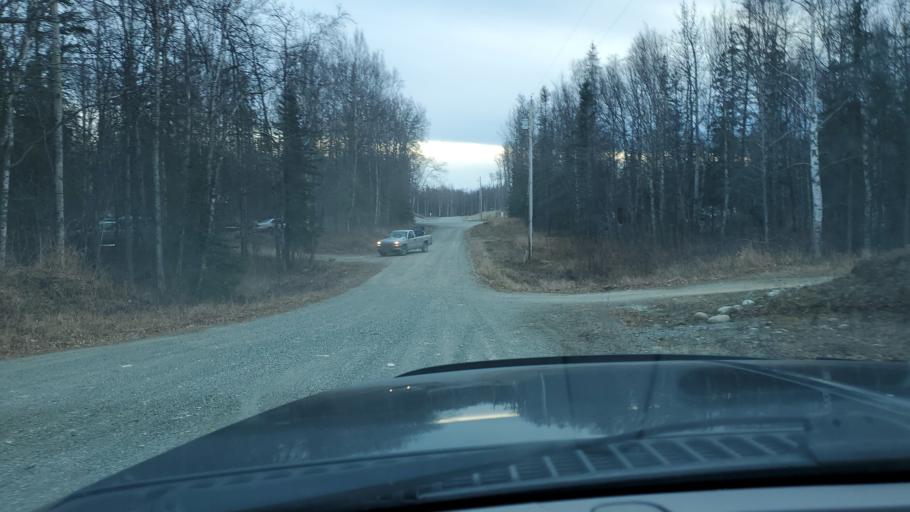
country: US
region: Alaska
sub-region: Matanuska-Susitna Borough
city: Lakes
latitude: 61.6586
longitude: -149.3037
